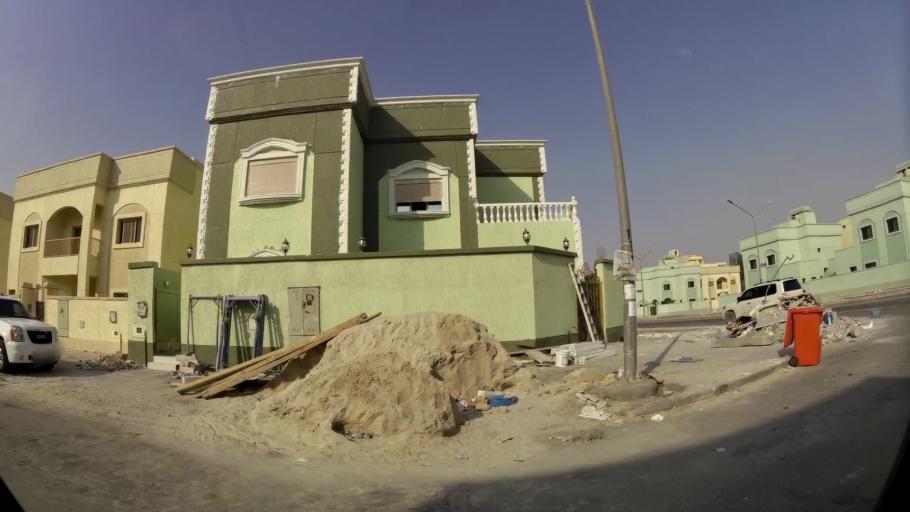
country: KW
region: Al Asimah
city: Ar Rabiyah
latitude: 29.3317
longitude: 47.8080
